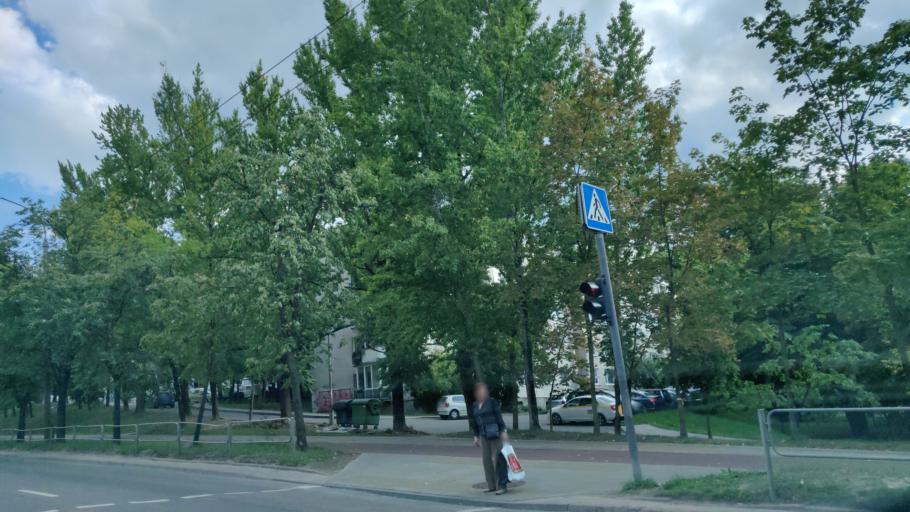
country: LT
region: Vilnius County
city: Vilkpede
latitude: 54.6736
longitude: 25.2542
